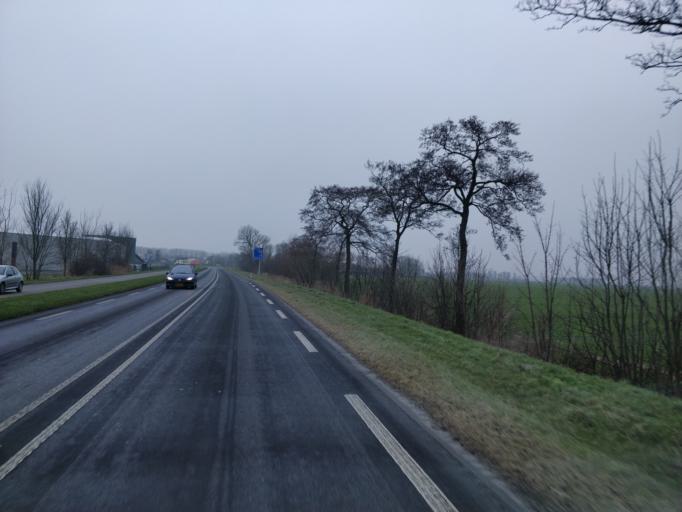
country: NL
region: Friesland
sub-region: Menameradiel
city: Berltsum
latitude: 53.2398
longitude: 5.6735
